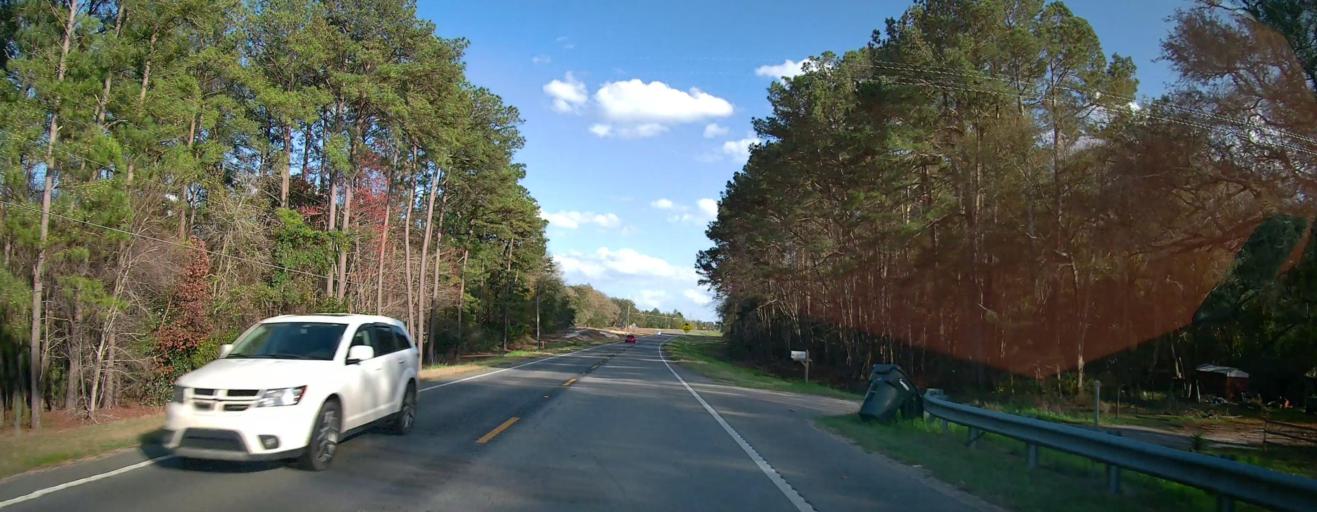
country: US
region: Georgia
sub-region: Tattnall County
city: Reidsville
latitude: 32.1168
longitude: -82.1881
